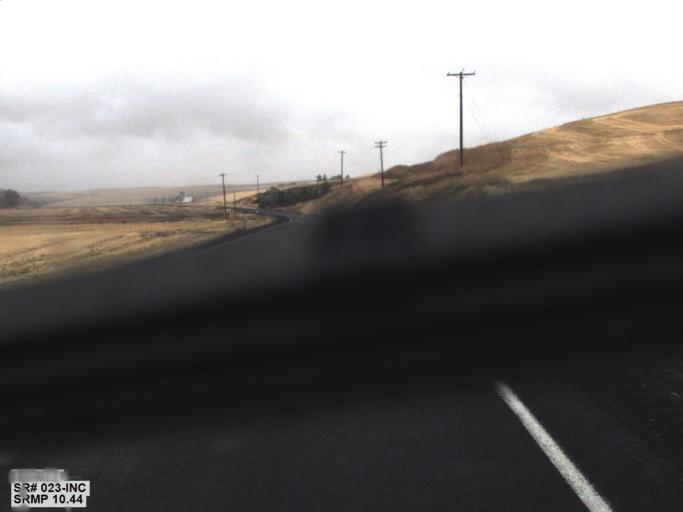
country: US
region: Washington
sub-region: Whitman County
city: Colfax
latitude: 47.0614
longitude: -117.5235
